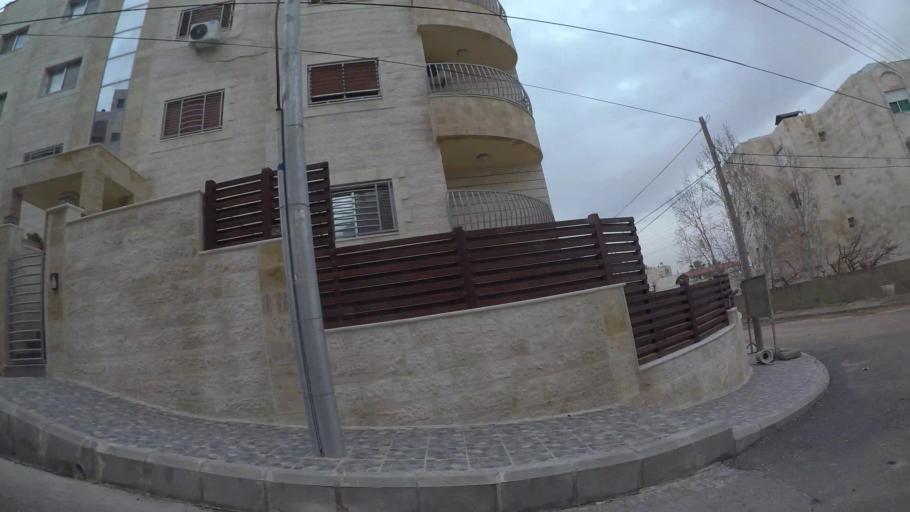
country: JO
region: Amman
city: Umm as Summaq
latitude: 31.8972
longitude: 35.8459
